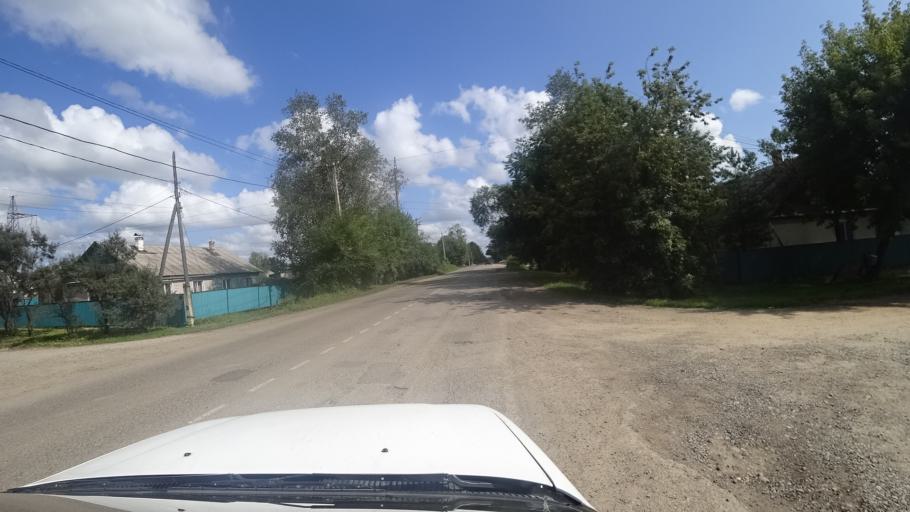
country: RU
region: Primorskiy
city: Dal'nerechensk
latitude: 45.9273
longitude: 133.7668
